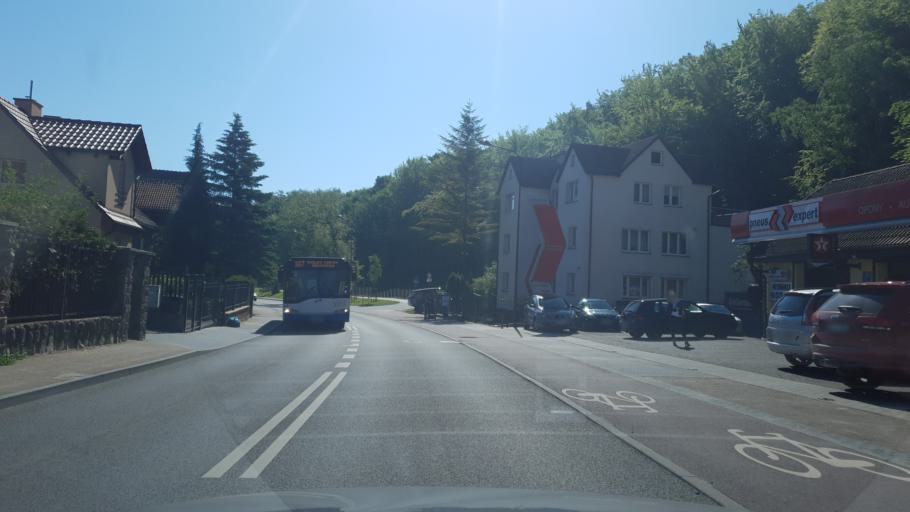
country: PL
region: Pomeranian Voivodeship
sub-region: Sopot
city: Sopot
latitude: 54.4553
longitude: 18.5448
